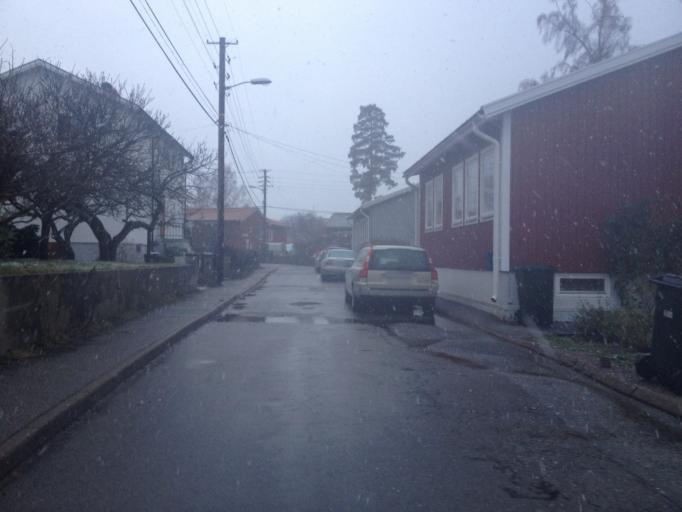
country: SE
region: Stockholm
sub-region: Stockholms Kommun
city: Bromma
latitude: 59.3533
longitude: 17.8994
